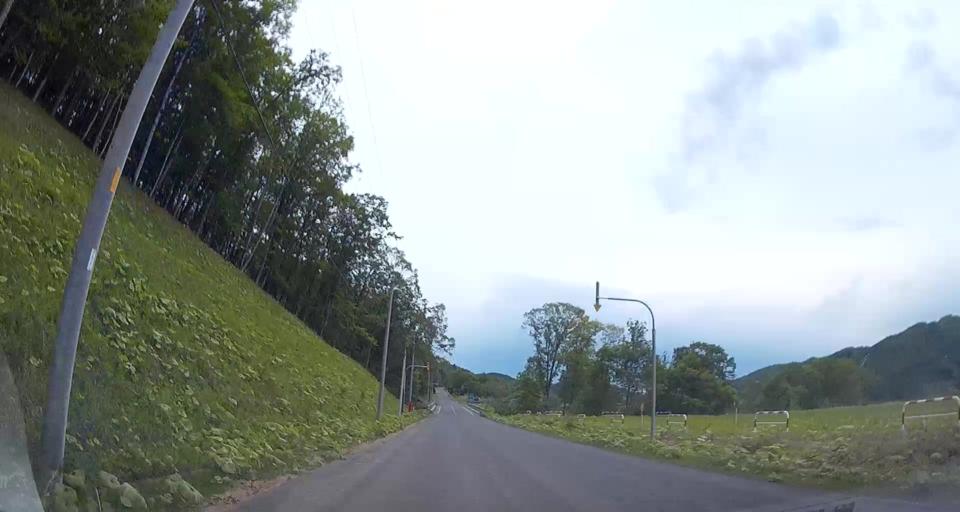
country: JP
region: Hokkaido
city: Chitose
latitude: 42.7772
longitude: 142.0101
